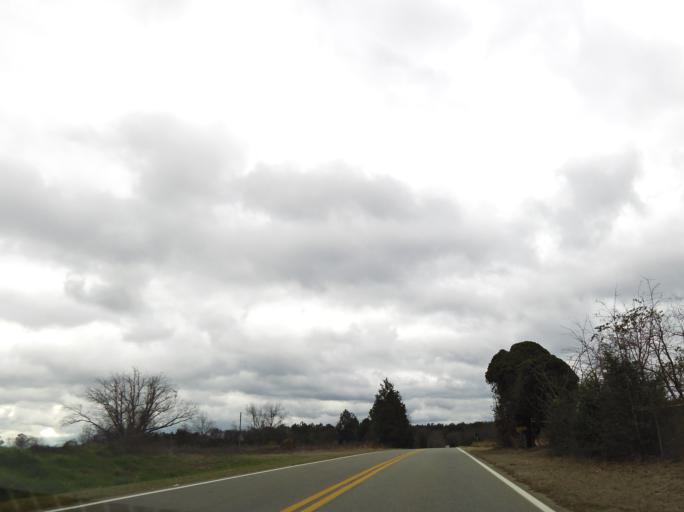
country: US
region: Georgia
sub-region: Twiggs County
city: Jeffersonville
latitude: 32.5708
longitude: -83.3774
